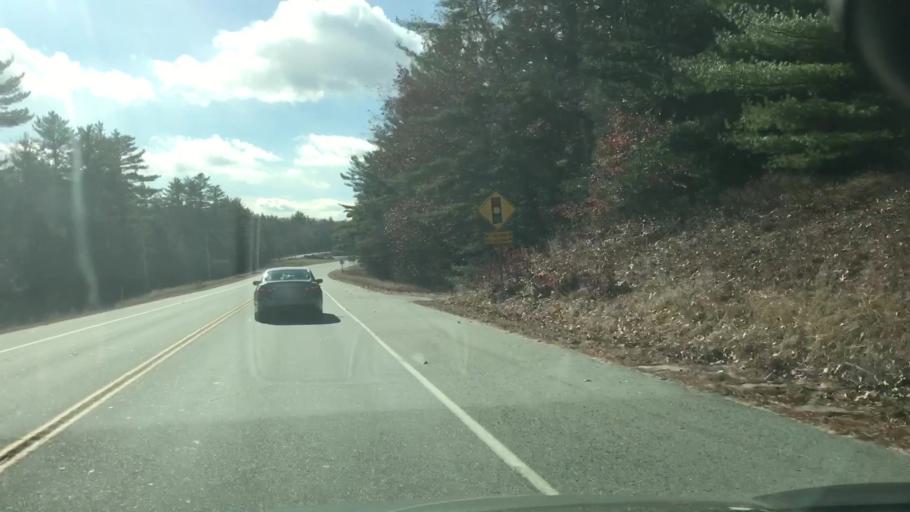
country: US
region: New Hampshire
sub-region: Belknap County
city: Barnstead
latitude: 43.3475
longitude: -71.2649
